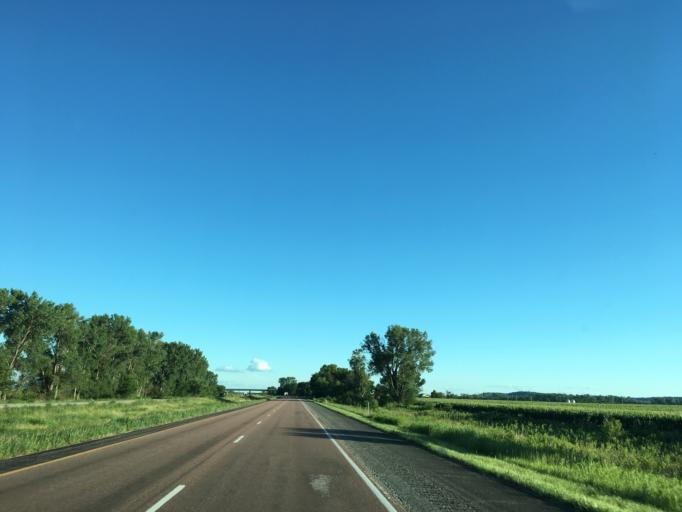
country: US
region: Nebraska
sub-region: Cass County
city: Plattsmouth
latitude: 40.9526
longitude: -95.8006
